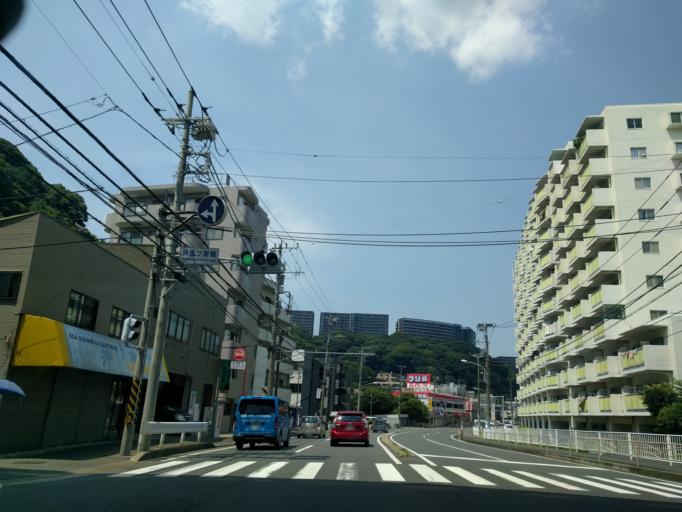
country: JP
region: Kanagawa
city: Yokohama
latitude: 35.3968
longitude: 139.6142
